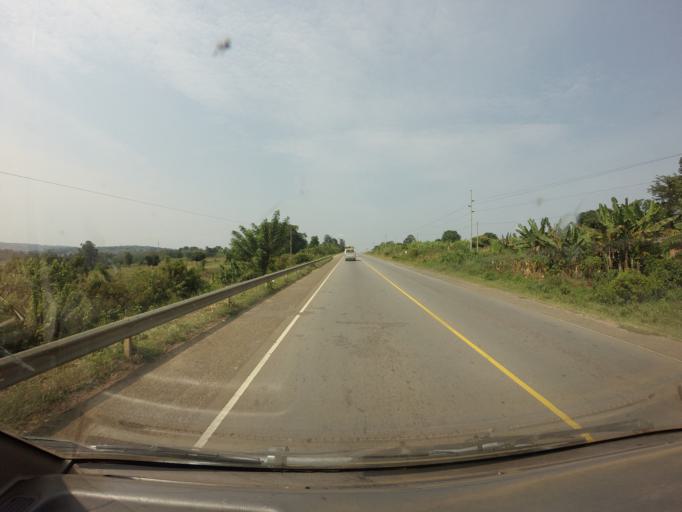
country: UG
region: Central Region
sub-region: Lwengo District
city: Lwengo
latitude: -0.3968
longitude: 31.4258
